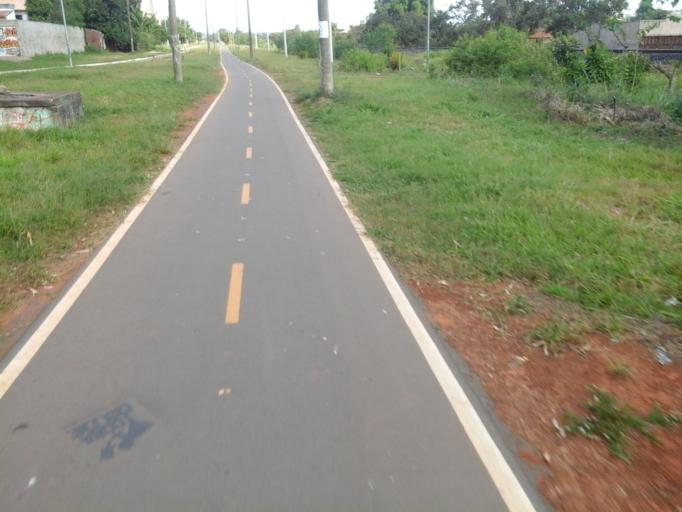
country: BR
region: Federal District
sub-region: Brasilia
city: Brasilia
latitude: -15.8213
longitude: -47.9919
